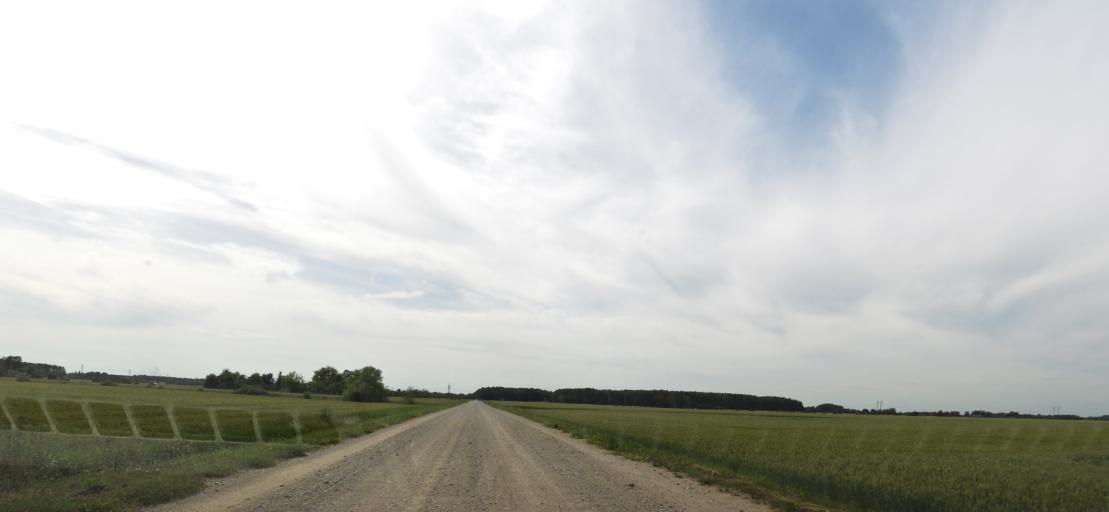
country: LT
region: Panevezys
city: Pasvalys
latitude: 55.9655
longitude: 24.3274
